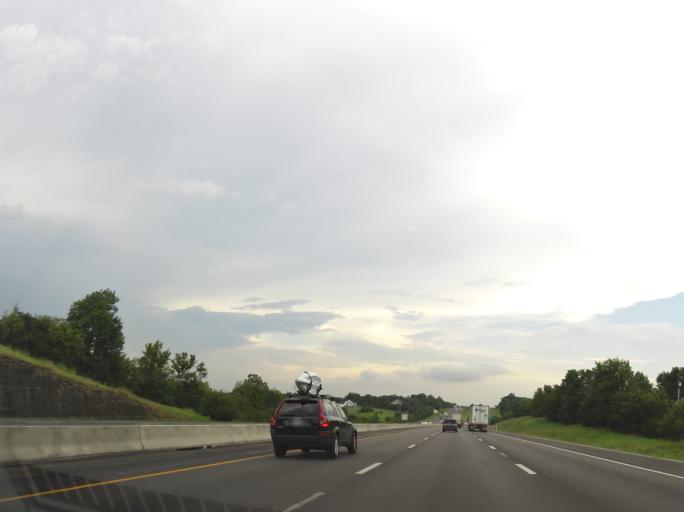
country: US
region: Kentucky
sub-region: Madison County
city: Richmond
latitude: 37.7022
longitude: -84.3181
